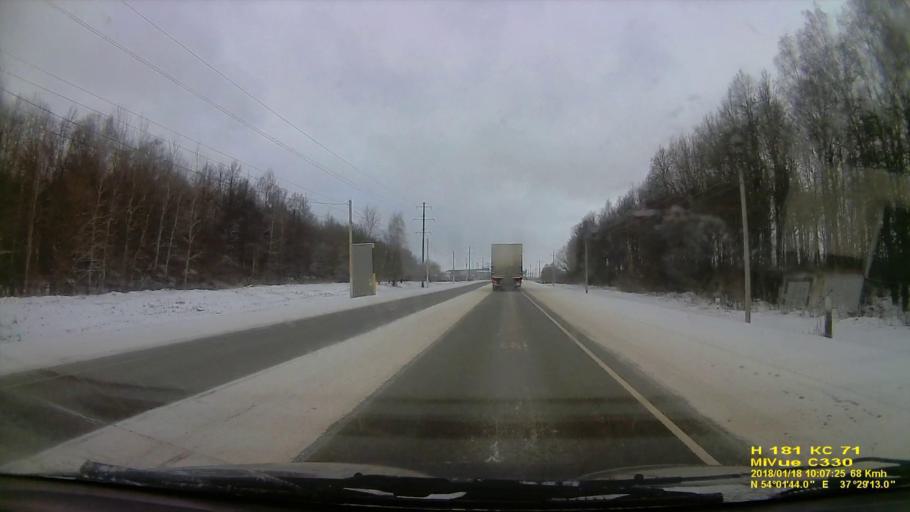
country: RU
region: Tula
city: Pervomayskiy
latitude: 54.0286
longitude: 37.4869
